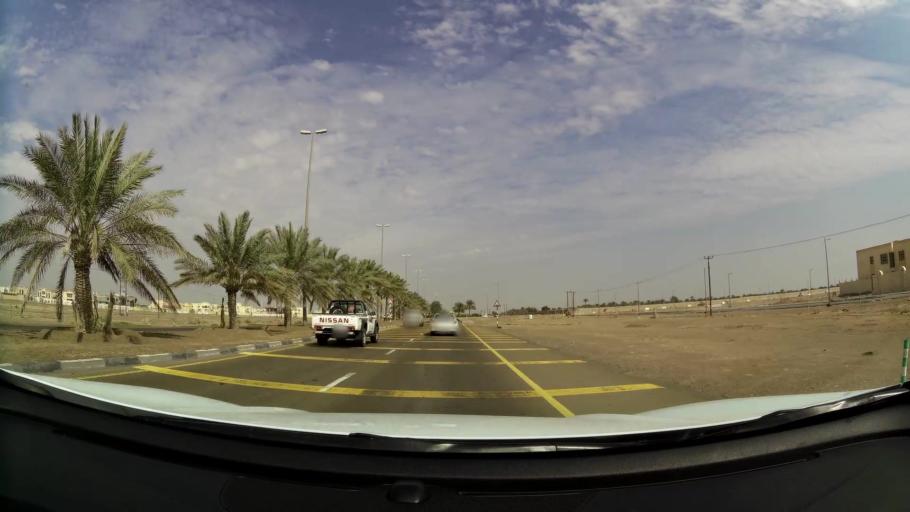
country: AE
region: Abu Dhabi
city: Al Ain
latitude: 24.0893
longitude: 55.8497
